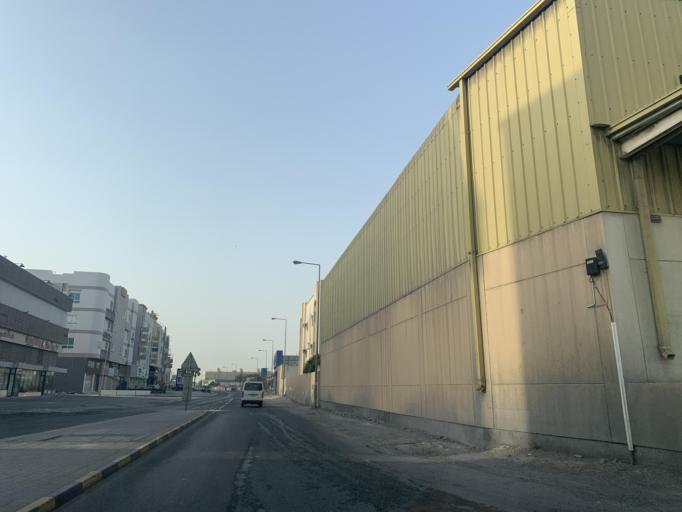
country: BH
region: Northern
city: Madinat `Isa
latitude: 26.1917
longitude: 50.5564
